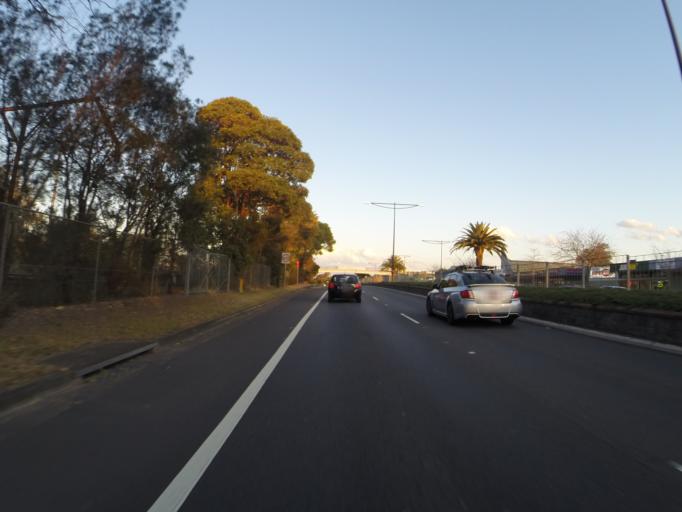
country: AU
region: New South Wales
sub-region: Blue Mountains Municipality
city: Blaxland
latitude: -33.7429
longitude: 150.6084
